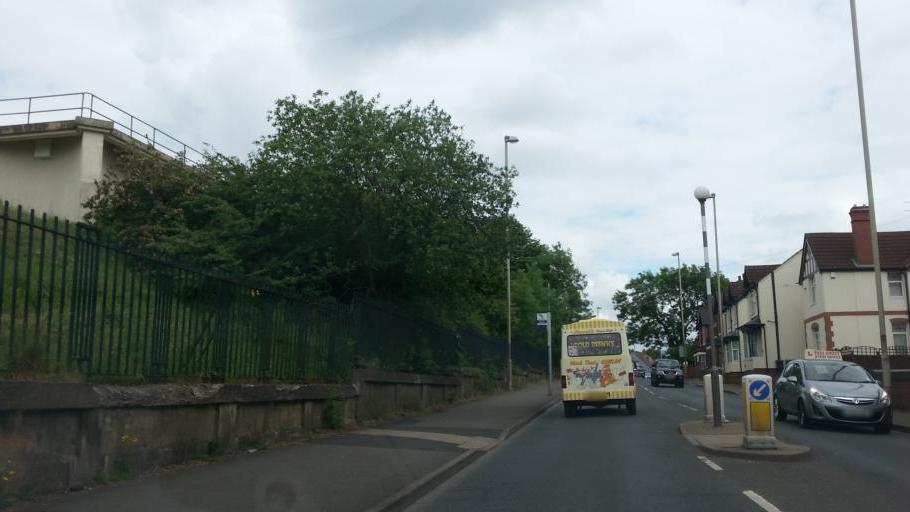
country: GB
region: England
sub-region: Dudley
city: Dudley
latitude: 52.5183
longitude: -2.1016
